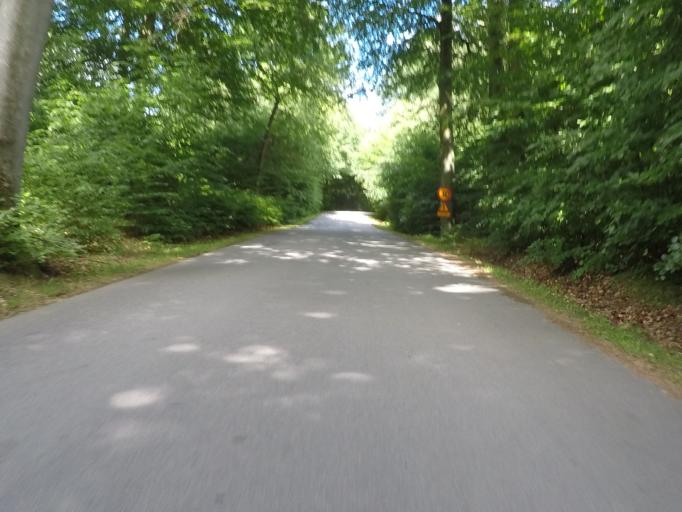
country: SE
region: Skane
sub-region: Svedala Kommun
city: Svedala
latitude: 55.5513
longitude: 13.2241
